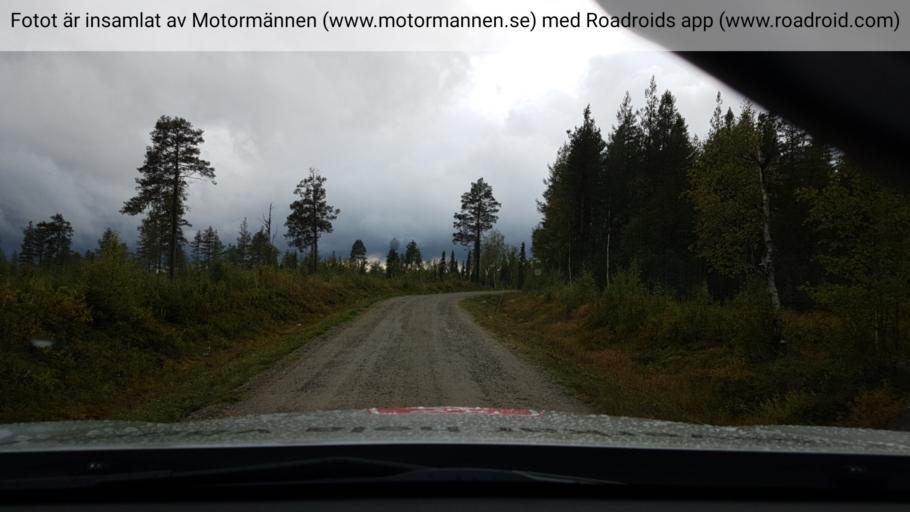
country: SE
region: Vaesterbotten
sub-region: Asele Kommun
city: Asele
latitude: 64.1462
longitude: 16.9095
